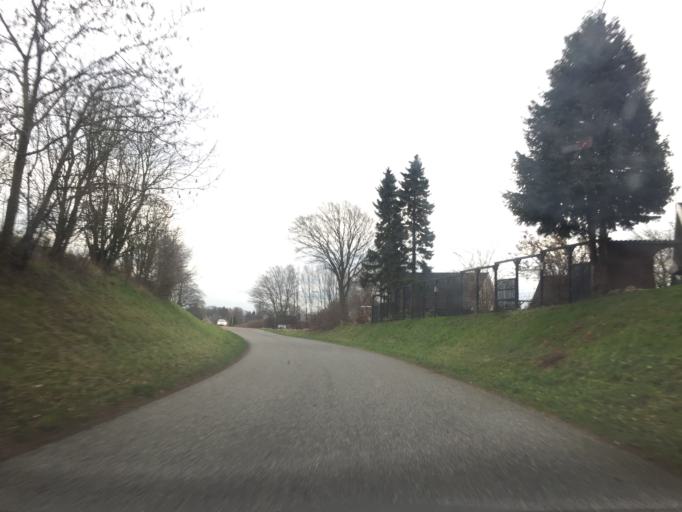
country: DK
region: South Denmark
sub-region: Nyborg Kommune
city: Nyborg
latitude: 55.1974
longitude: 10.7258
